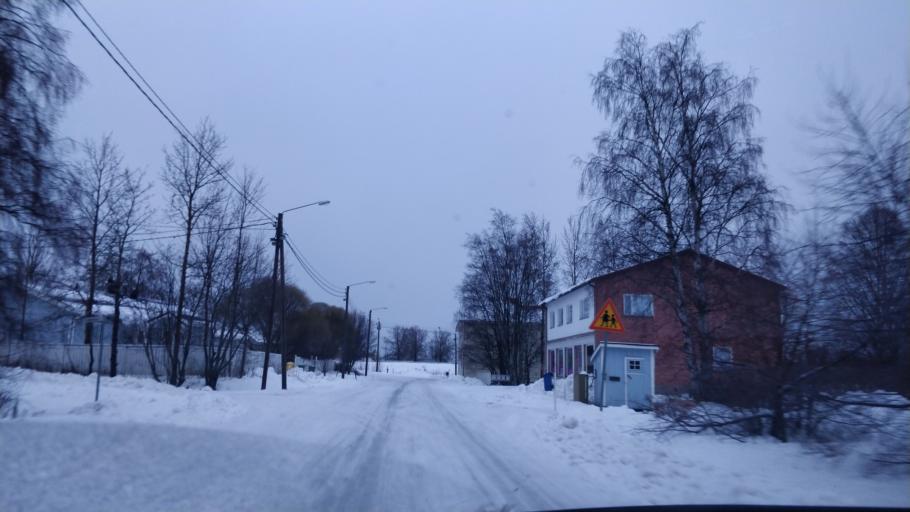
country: FI
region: Lapland
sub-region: Kemi-Tornio
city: Kemi
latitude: 65.7456
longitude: 24.5766
